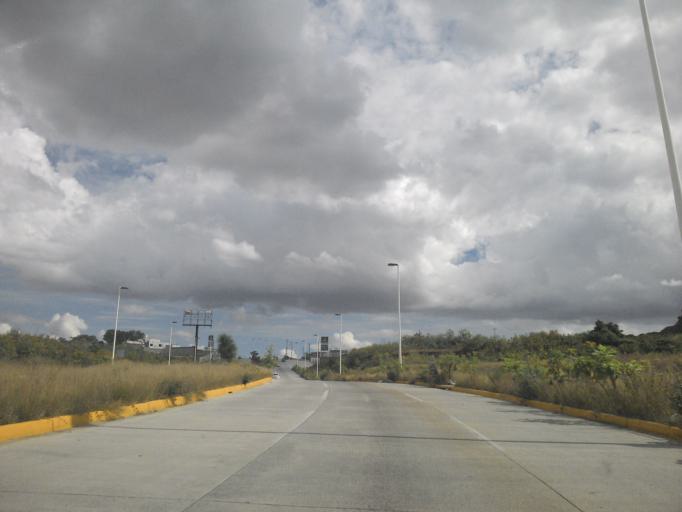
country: MX
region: Jalisco
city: Guadalajara
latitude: 20.6670
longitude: -103.4596
